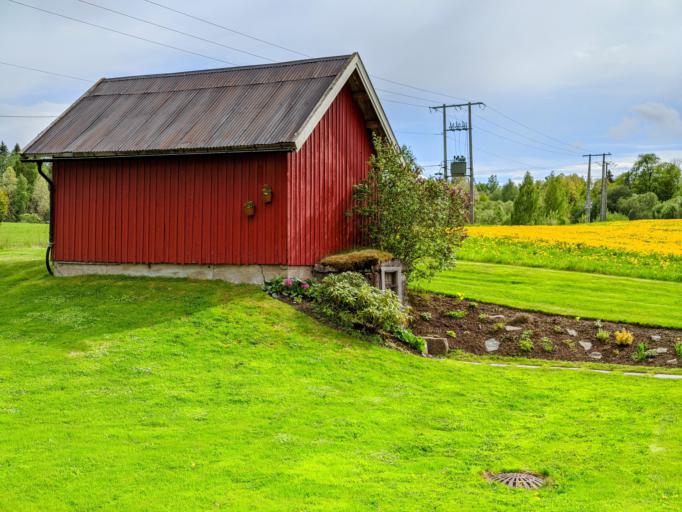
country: NO
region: Akershus
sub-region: Gjerdrum
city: Ask
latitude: 60.1431
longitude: 11.0236
